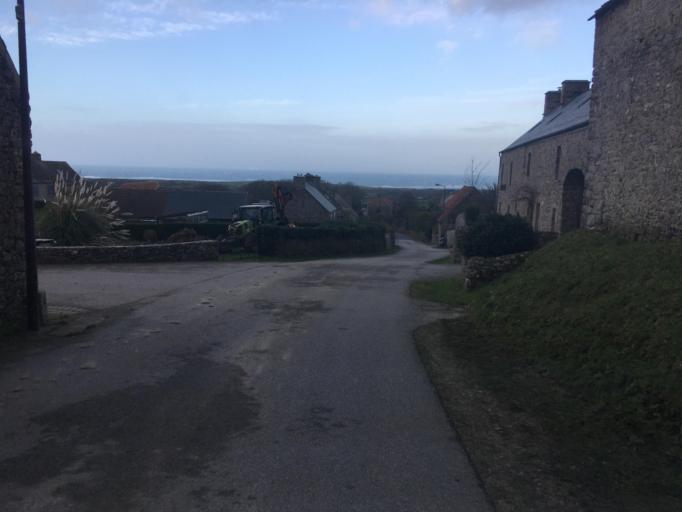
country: FR
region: Lower Normandy
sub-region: Departement de la Manche
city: Beaumont-Hague
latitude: 49.7121
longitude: -1.9221
